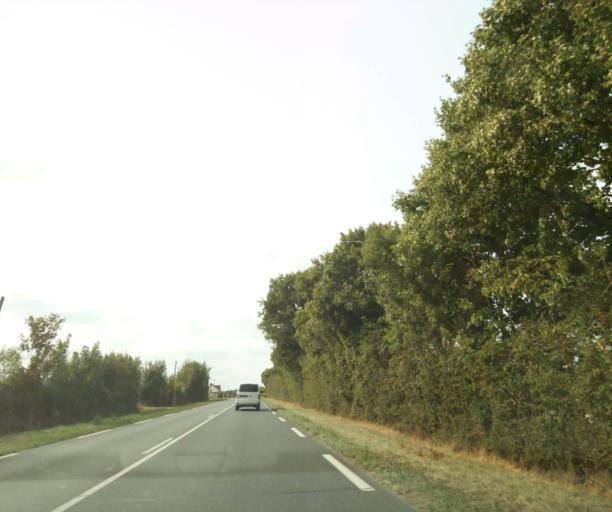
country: FR
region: Centre
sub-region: Departement de l'Indre
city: Chatillon-sur-Indre
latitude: 46.9721
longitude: 1.1910
